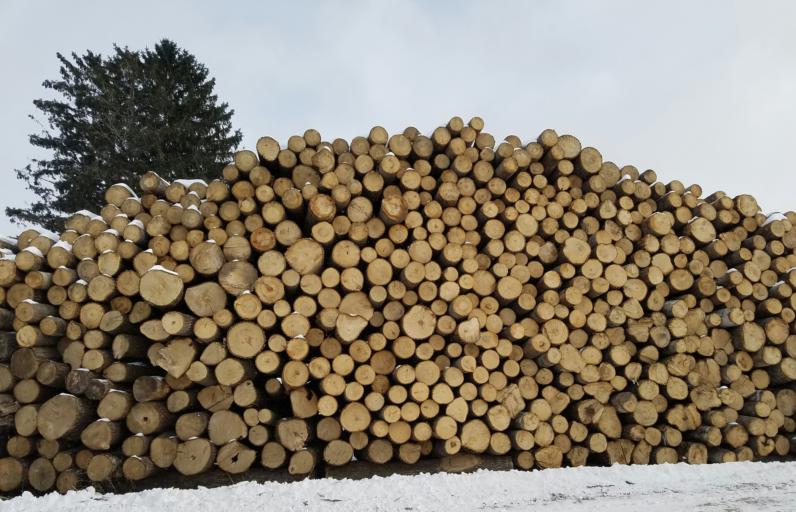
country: US
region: Wisconsin
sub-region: Clark County
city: Loyal
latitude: 44.6603
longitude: -90.4807
